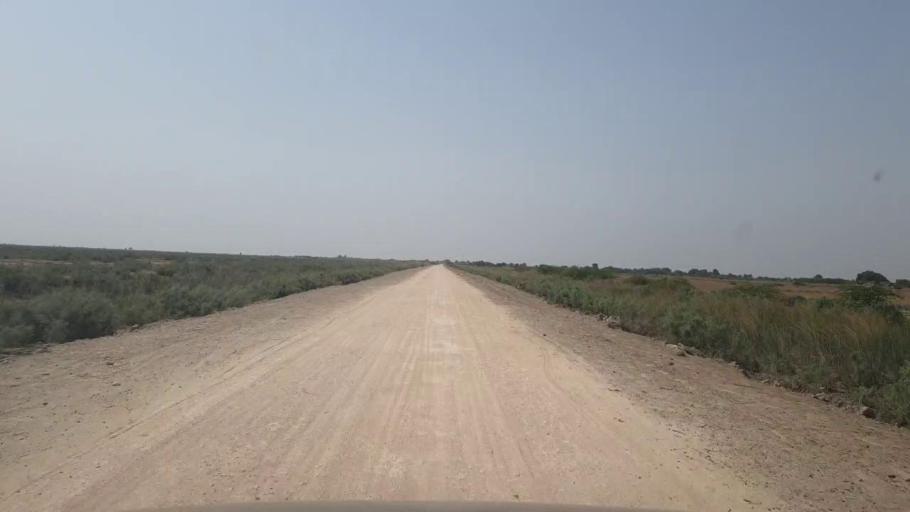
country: PK
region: Sindh
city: Jati
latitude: 24.3695
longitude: 68.5630
